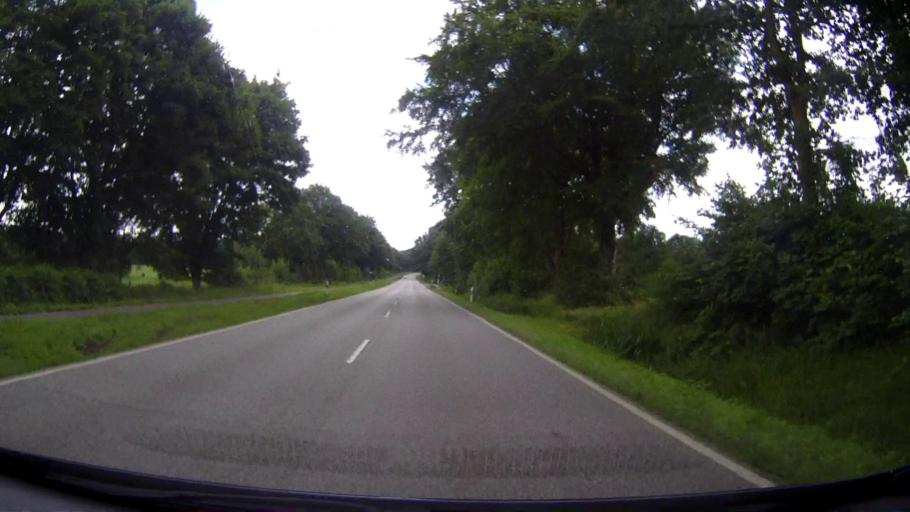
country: DE
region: Schleswig-Holstein
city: Meezen
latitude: 54.0770
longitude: 9.7175
